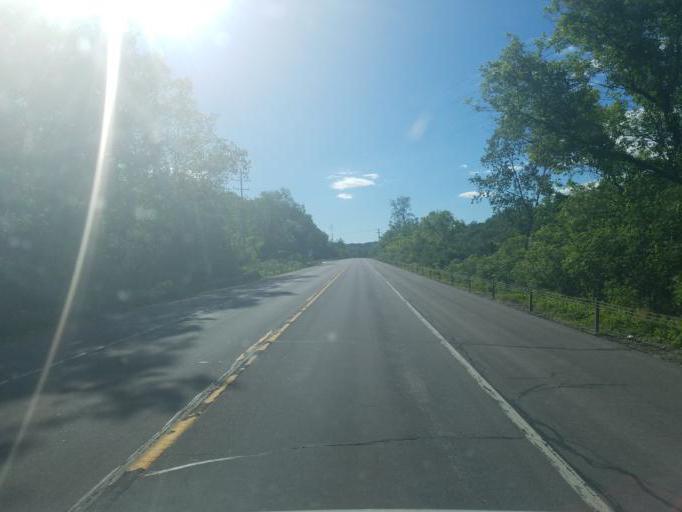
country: US
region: New York
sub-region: Herkimer County
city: Little Falls
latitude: 43.0326
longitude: -74.8289
